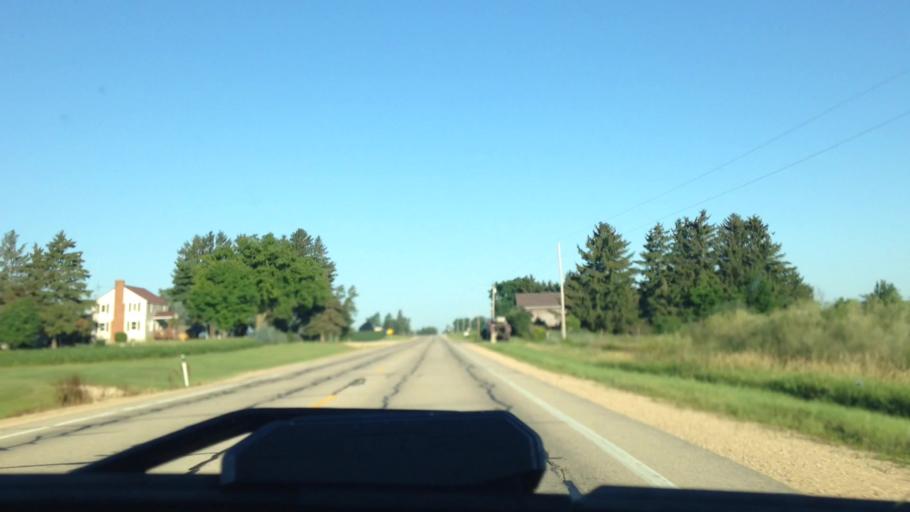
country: US
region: Wisconsin
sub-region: Columbia County
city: Fall River
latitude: 43.3414
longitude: -89.0823
